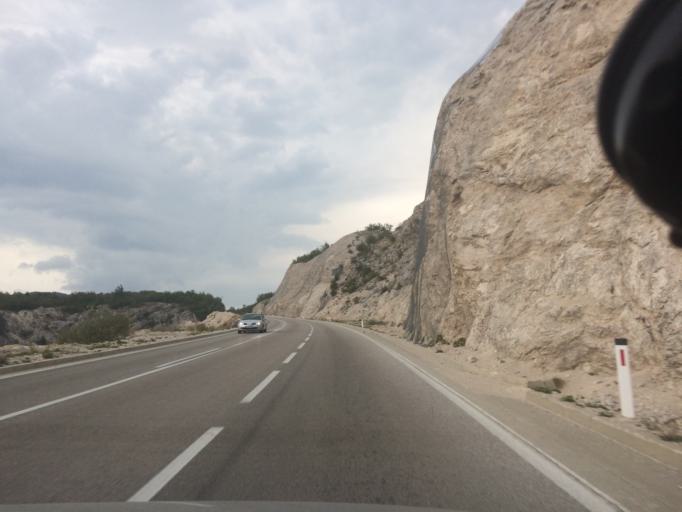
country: ME
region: Kotor
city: Risan
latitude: 42.6630
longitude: 18.6647
